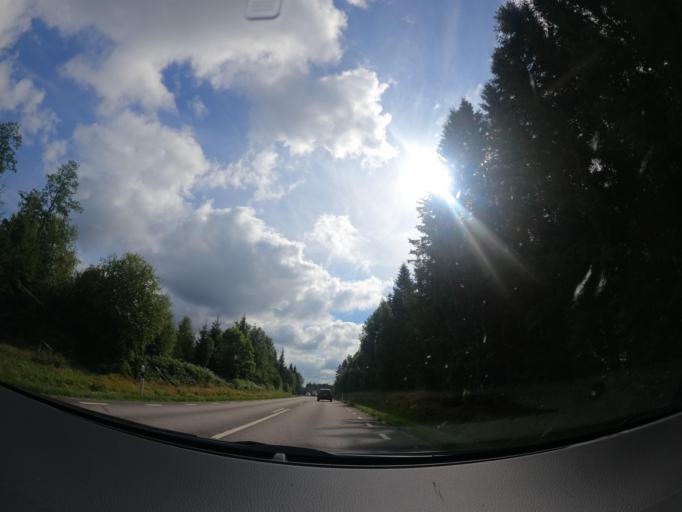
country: SE
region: Halland
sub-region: Hylte Kommun
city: Hyltebruk
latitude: 57.1298
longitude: 13.2262
